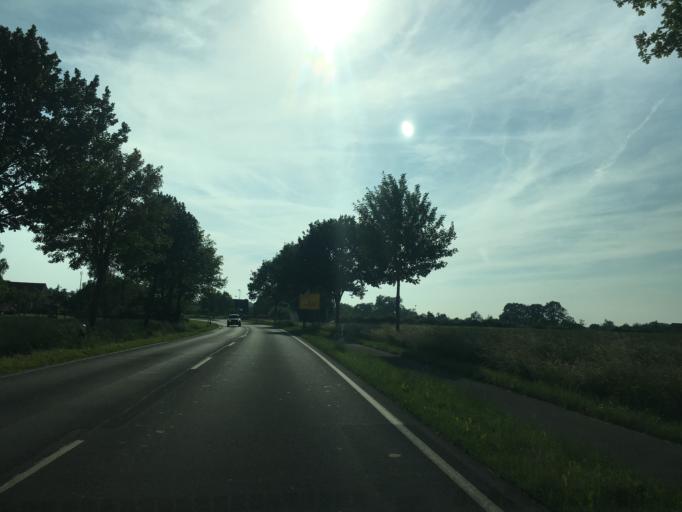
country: DE
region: North Rhine-Westphalia
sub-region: Regierungsbezirk Munster
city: Altenberge
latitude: 52.0524
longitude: 7.4888
